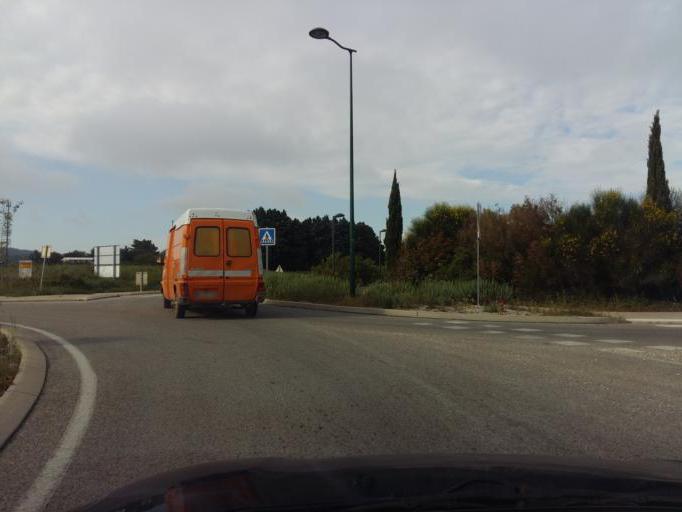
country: FR
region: Languedoc-Roussillon
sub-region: Departement du Gard
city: Saint-Genies-de-Comolas
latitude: 44.0593
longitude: 4.7123
